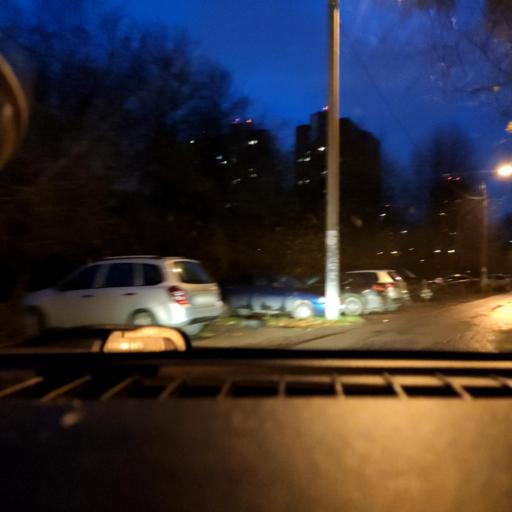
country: RU
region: Perm
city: Perm
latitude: 58.0001
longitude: 56.2157
